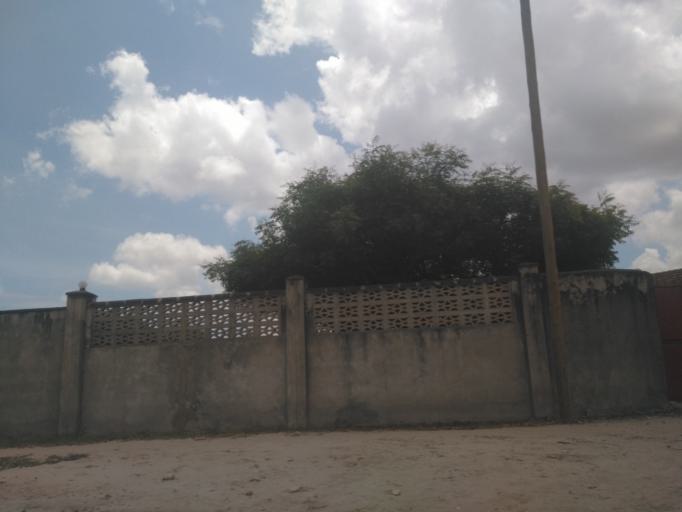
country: TZ
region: Dar es Salaam
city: Dar es Salaam
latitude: -6.8356
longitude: 39.2843
